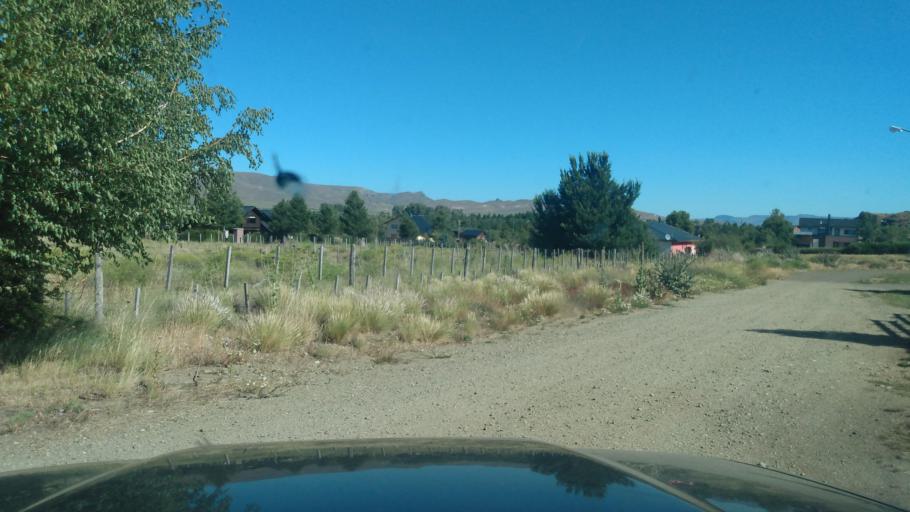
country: AR
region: Neuquen
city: Junin de los Andes
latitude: -39.9651
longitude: -71.0838
